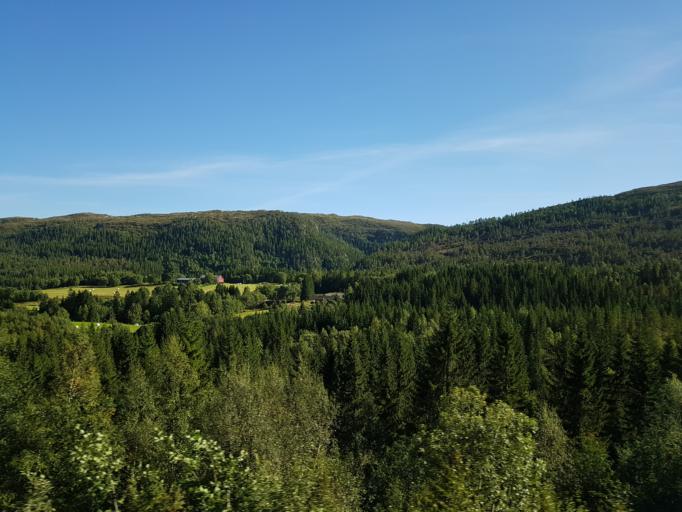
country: NO
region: Sor-Trondelag
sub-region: Afjord
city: A i Afjord
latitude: 63.7809
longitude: 10.2188
